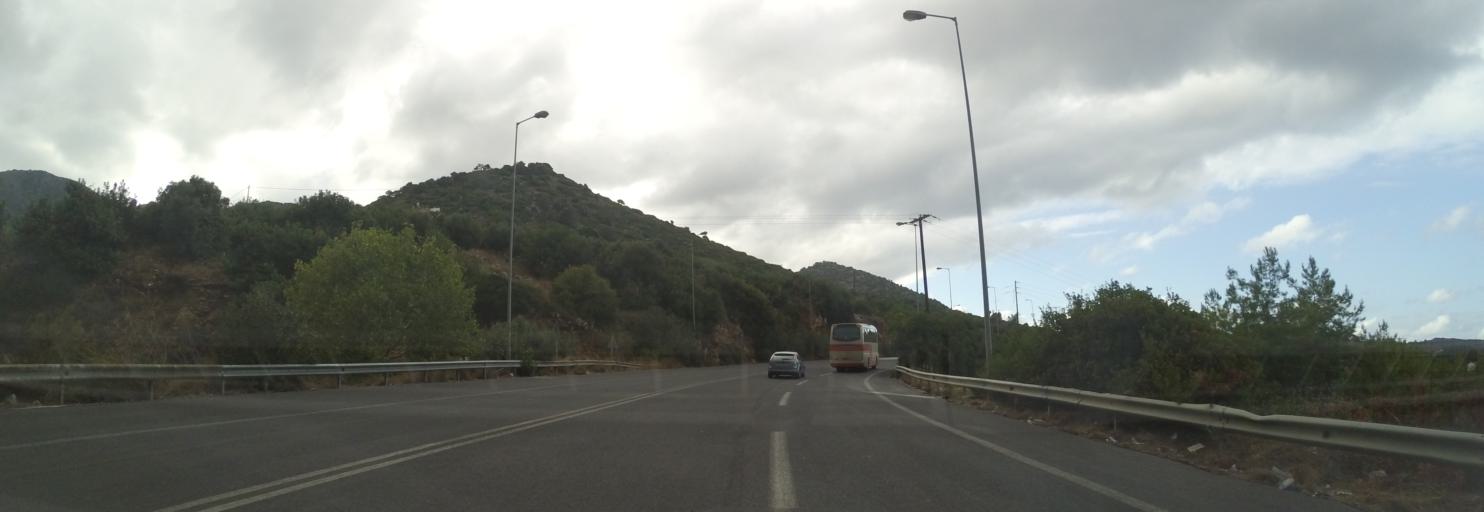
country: GR
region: Crete
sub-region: Nomos Rethymnis
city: Perama
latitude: 35.4013
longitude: 24.7843
